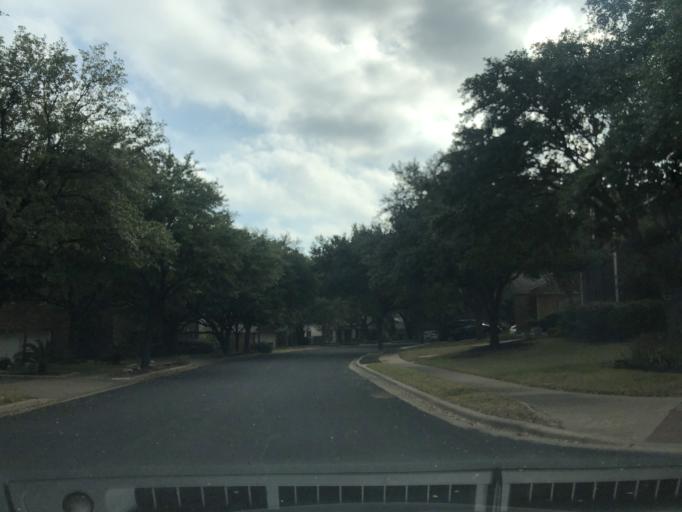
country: US
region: Texas
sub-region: Travis County
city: Wells Branch
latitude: 30.4188
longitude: -97.6825
